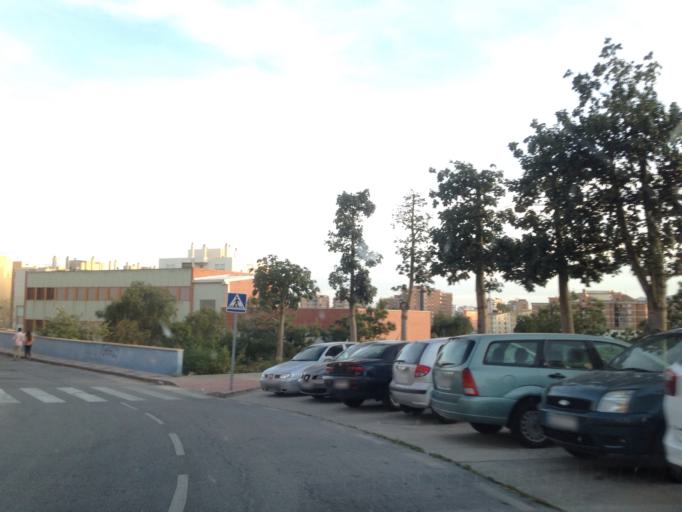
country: ES
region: Andalusia
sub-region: Provincia de Malaga
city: Malaga
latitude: 36.7271
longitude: -4.4460
